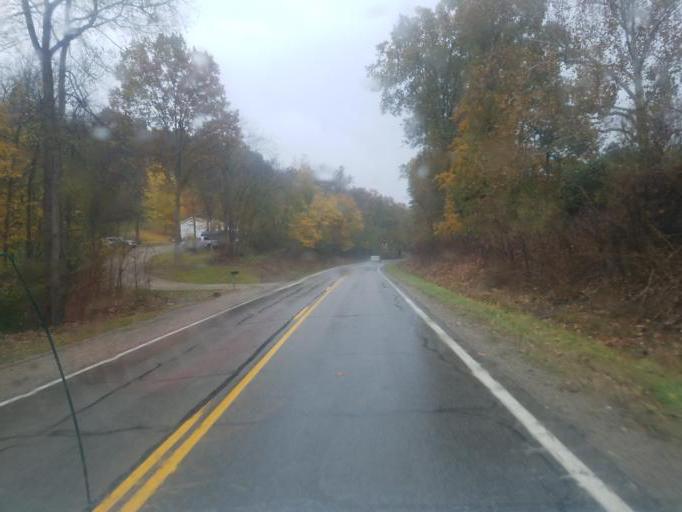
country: US
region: Ohio
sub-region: Muskingum County
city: South Zanesville
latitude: 39.8216
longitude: -81.8889
